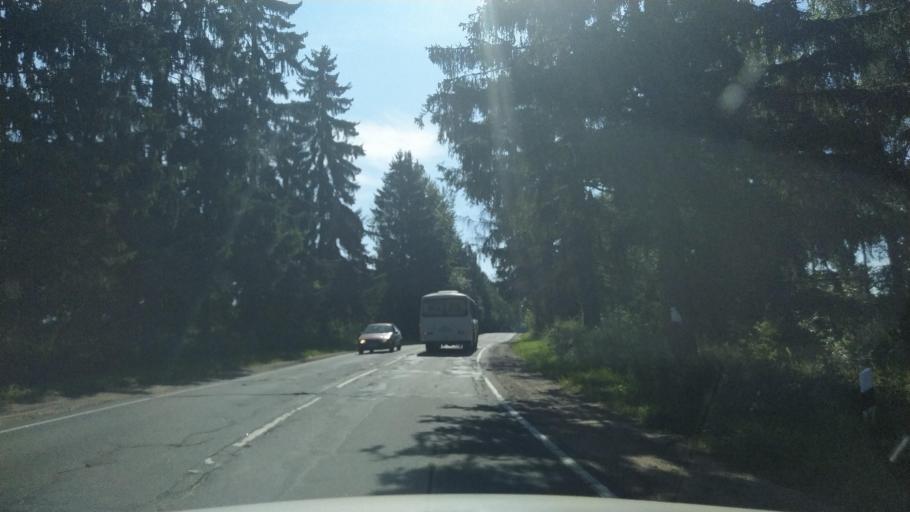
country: RU
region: Leningrad
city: Siverskiy
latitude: 59.3337
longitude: 30.0574
